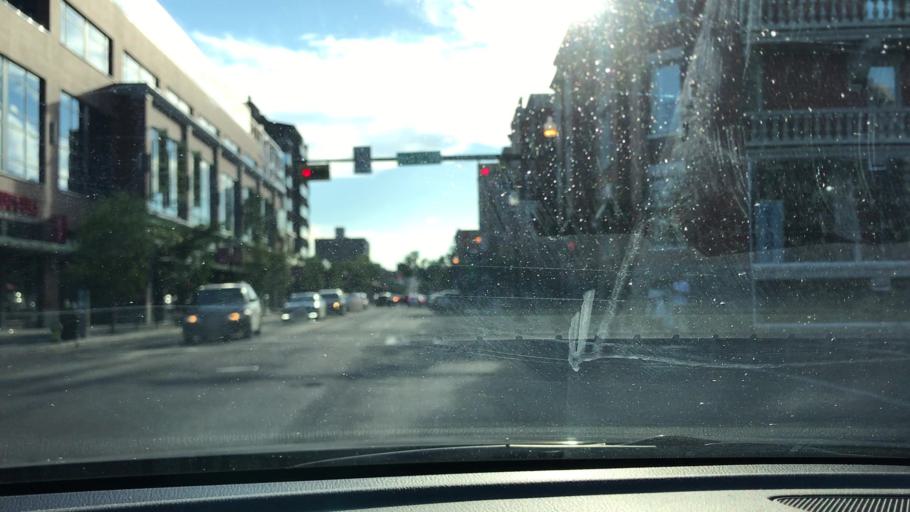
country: CA
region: Alberta
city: Calgary
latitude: 51.0379
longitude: -114.0817
